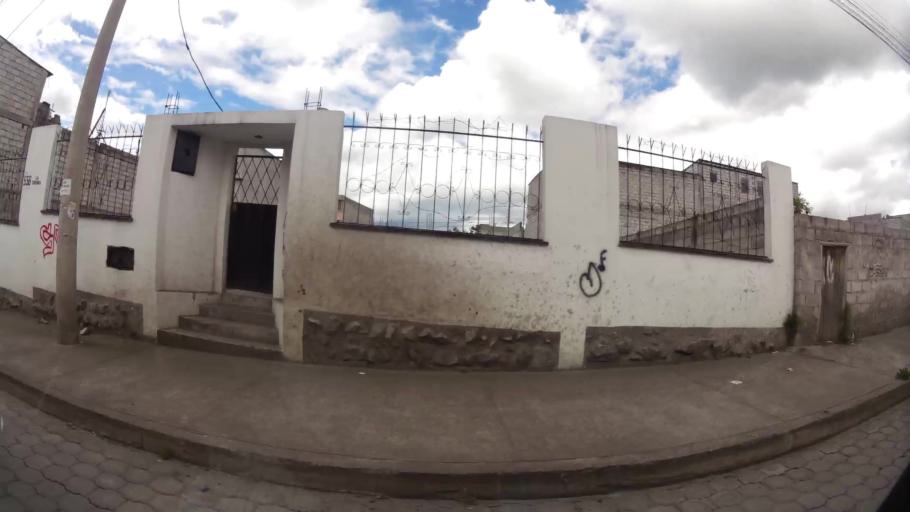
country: EC
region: Pichincha
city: Sangolqui
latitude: -0.3389
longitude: -78.5560
